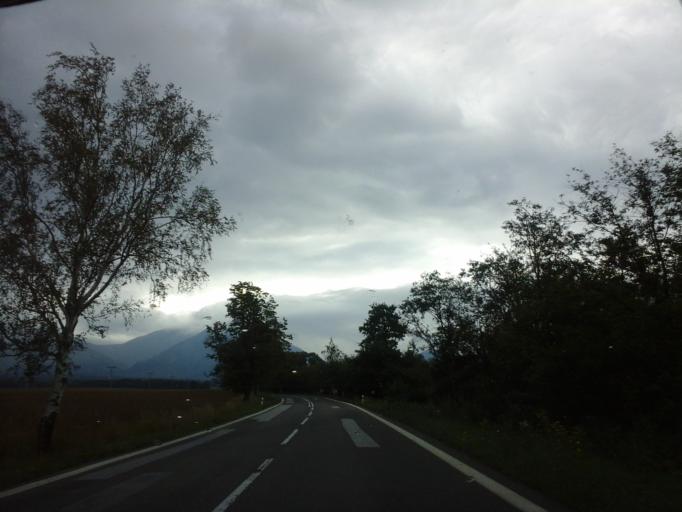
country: SK
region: Presovsky
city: Spisska Bela
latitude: 49.2027
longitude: 20.4087
